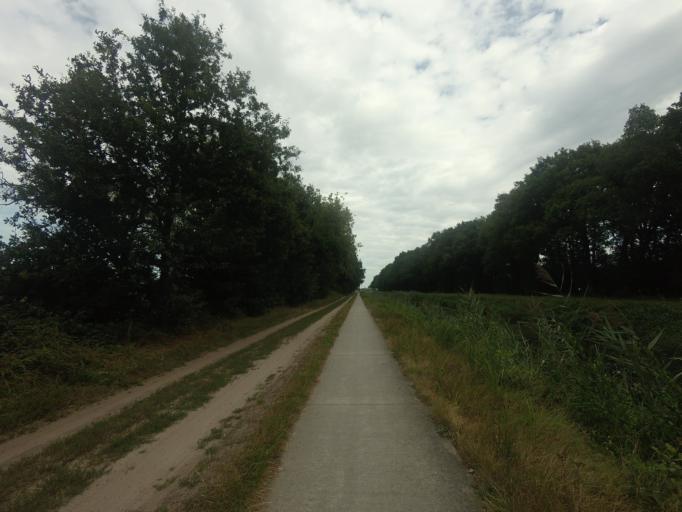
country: NL
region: Overijssel
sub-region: Gemeente Raalte
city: Raalte
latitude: 52.4379
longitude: 6.3312
